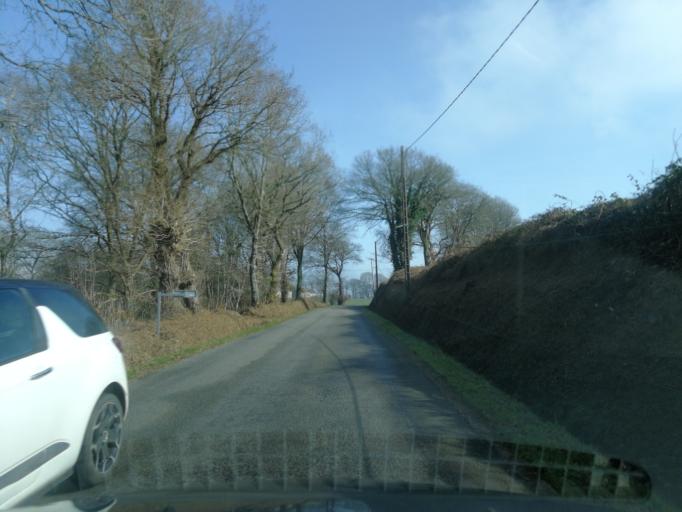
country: FR
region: Brittany
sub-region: Departement du Morbihan
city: La Vraie-Croix
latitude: 47.7090
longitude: -2.5105
